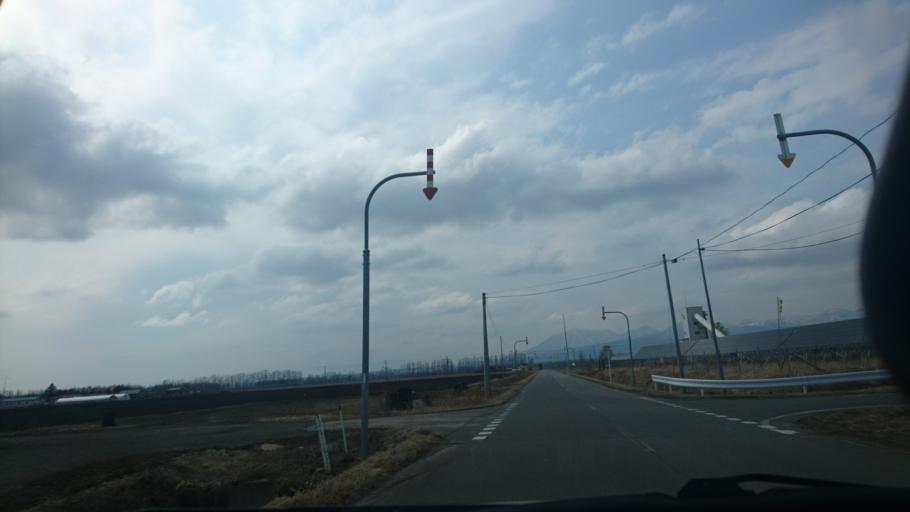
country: JP
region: Hokkaido
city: Otofuke
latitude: 43.2159
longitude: 143.2845
